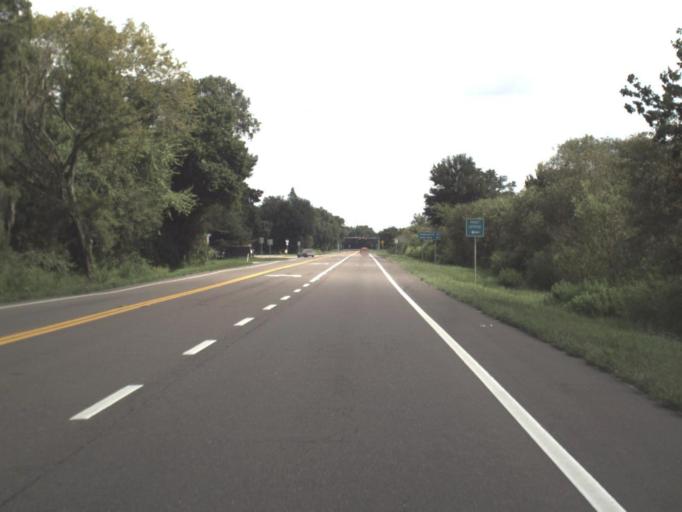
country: US
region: Florida
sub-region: Pasco County
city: Crystal Springs
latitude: 28.1772
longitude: -82.1571
